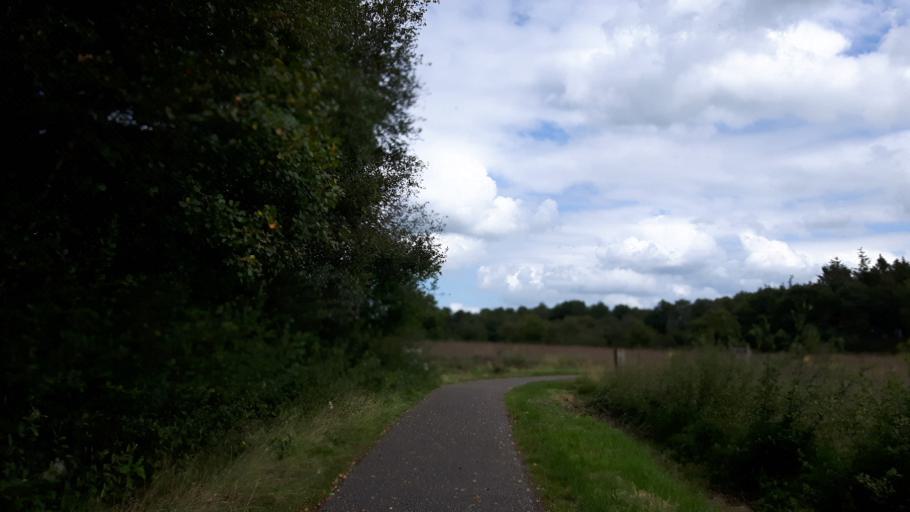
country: NL
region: Friesland
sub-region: Gemeente Smallingerland
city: Drachtstercompagnie
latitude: 53.0622
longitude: 6.2334
